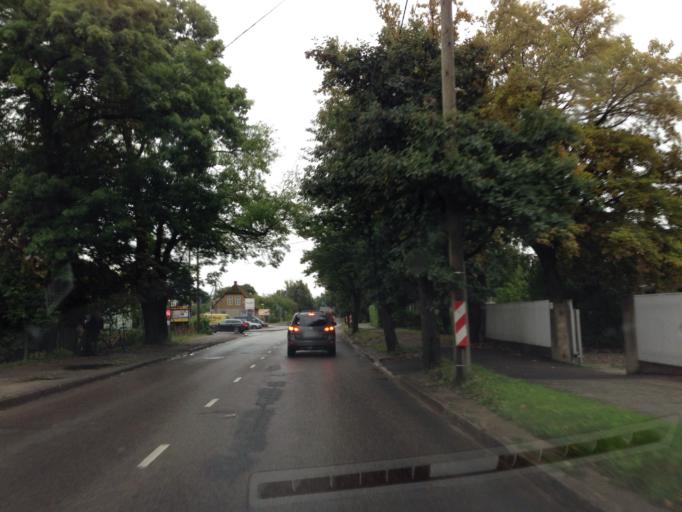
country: EE
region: Tartu
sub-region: Tartu linn
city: Tartu
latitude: 58.3622
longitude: 26.7212
